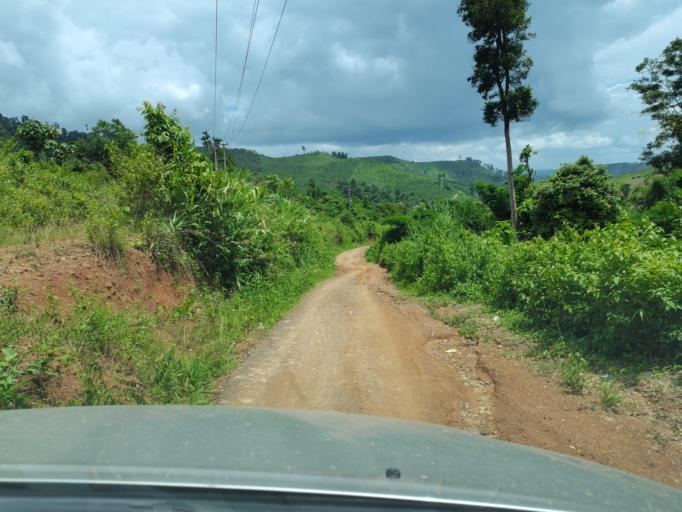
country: LA
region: Loungnamtha
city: Muang Long
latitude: 20.7286
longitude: 101.0140
